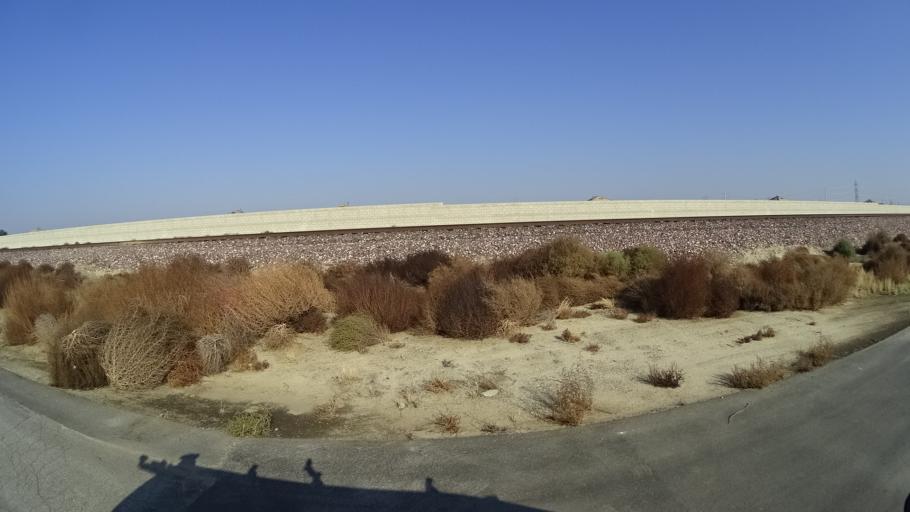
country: US
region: California
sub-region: Kern County
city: Greenacres
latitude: 35.3762
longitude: -119.1037
